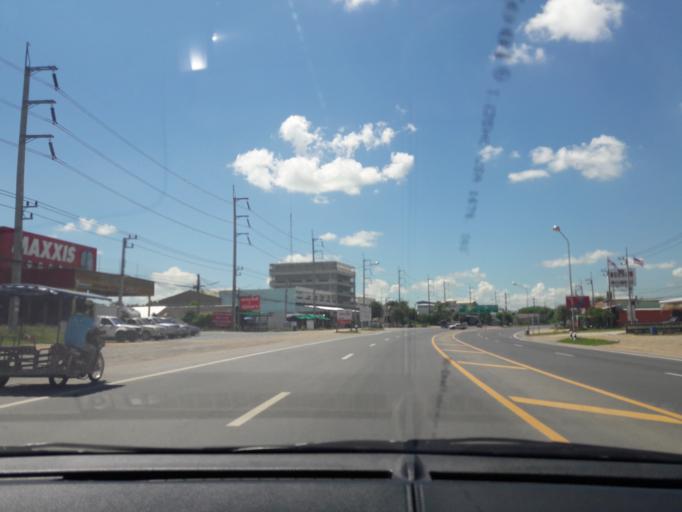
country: TH
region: Kanchanaburi
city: Tha Maka
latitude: 14.0368
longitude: 99.7938
